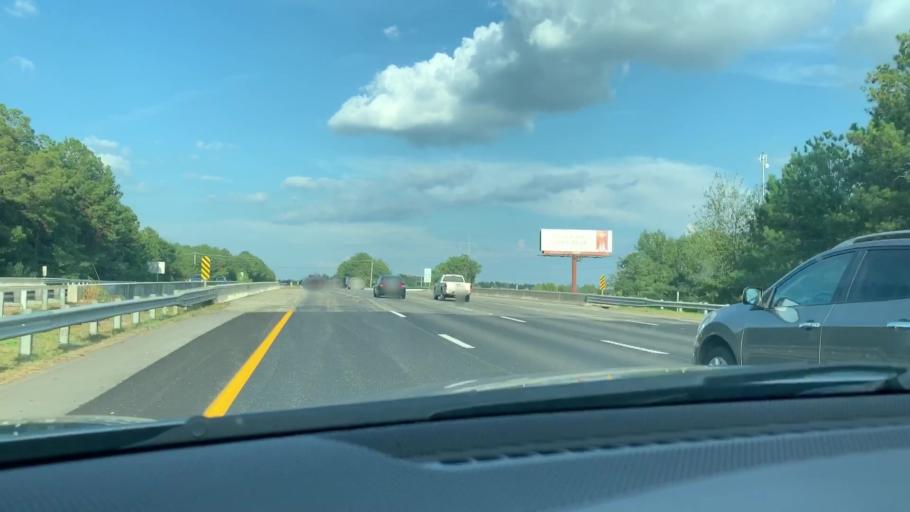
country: US
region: South Carolina
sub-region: Richland County
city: Forest Acres
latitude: 33.9527
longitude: -80.9649
